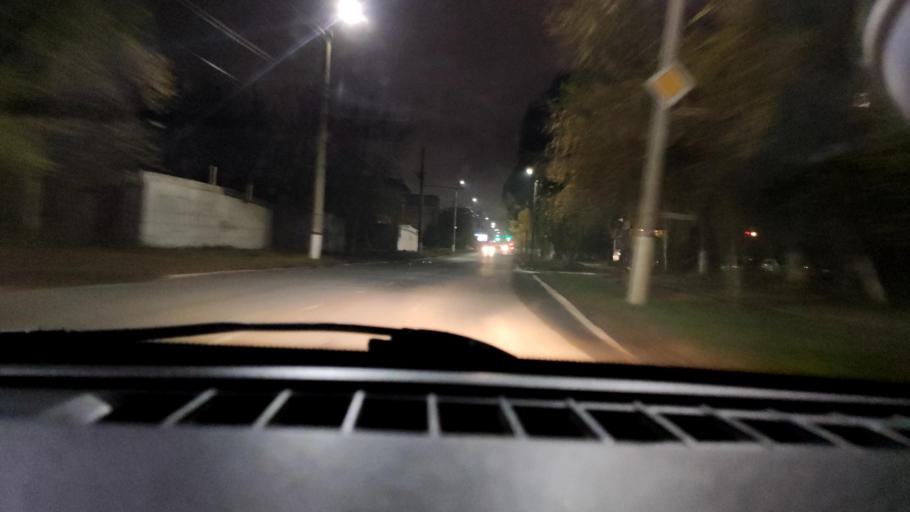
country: RU
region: Samara
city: Novokuybyshevsk
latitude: 53.1067
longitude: 49.9573
